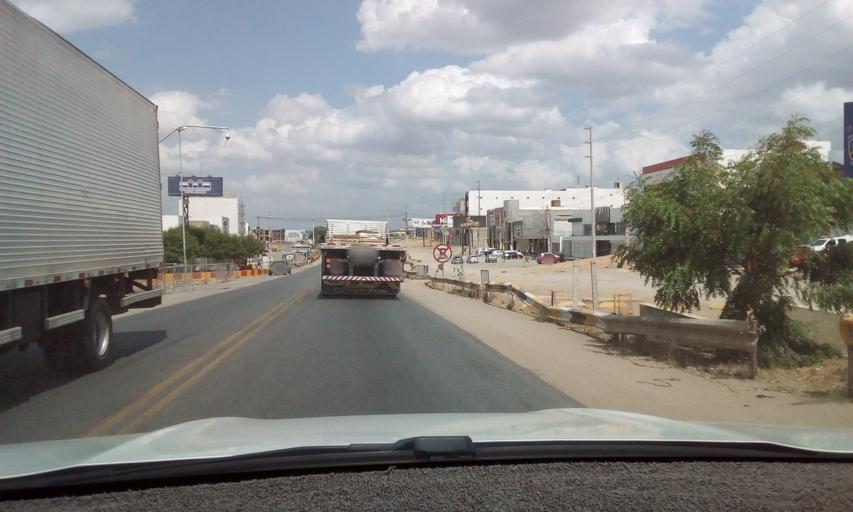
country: BR
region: Pernambuco
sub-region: Toritama
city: Toritama
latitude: -8.0073
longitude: -36.0655
